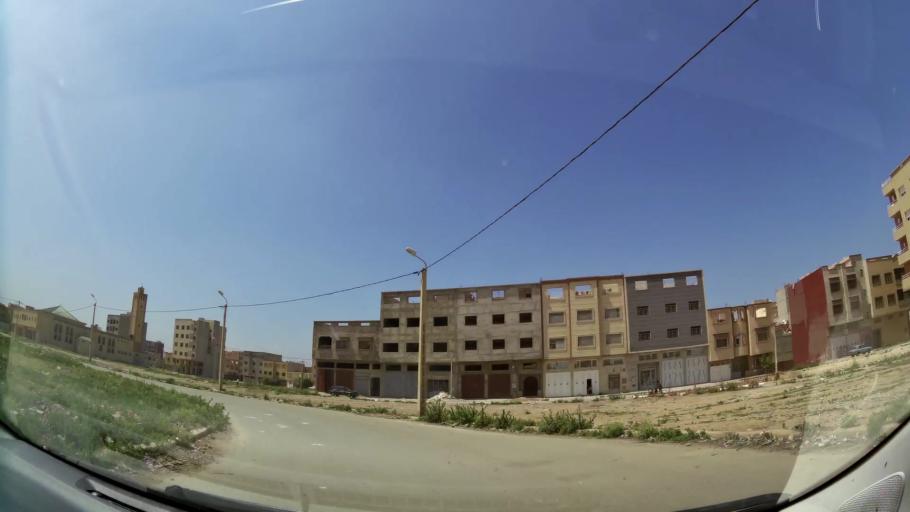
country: MA
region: Oriental
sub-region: Oujda-Angad
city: Oujda
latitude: 34.7006
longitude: -1.8865
